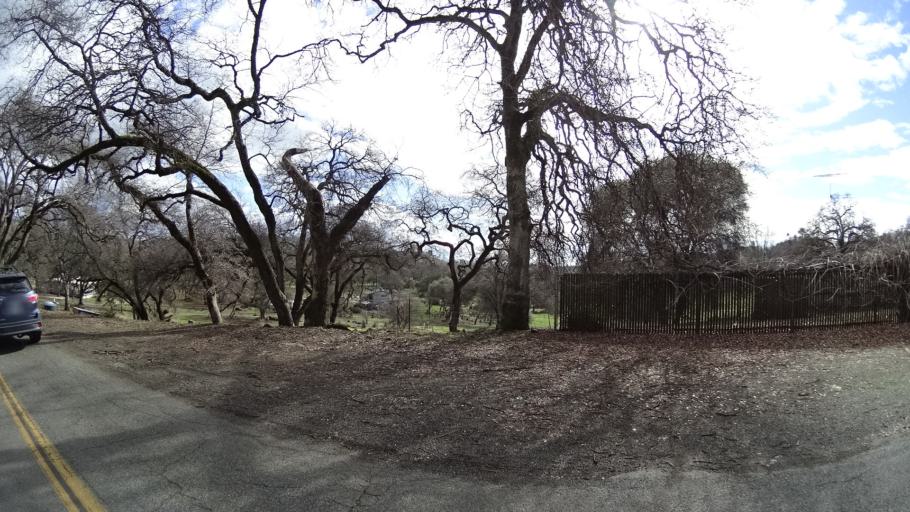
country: US
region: California
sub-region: Butte County
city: Oroville
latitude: 39.5973
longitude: -121.5377
